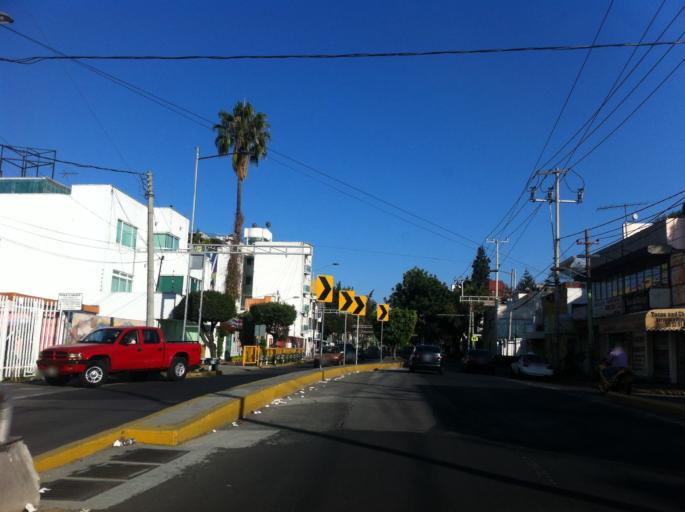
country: MX
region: Mexico City
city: Mexico City
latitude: 19.4136
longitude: -99.1116
